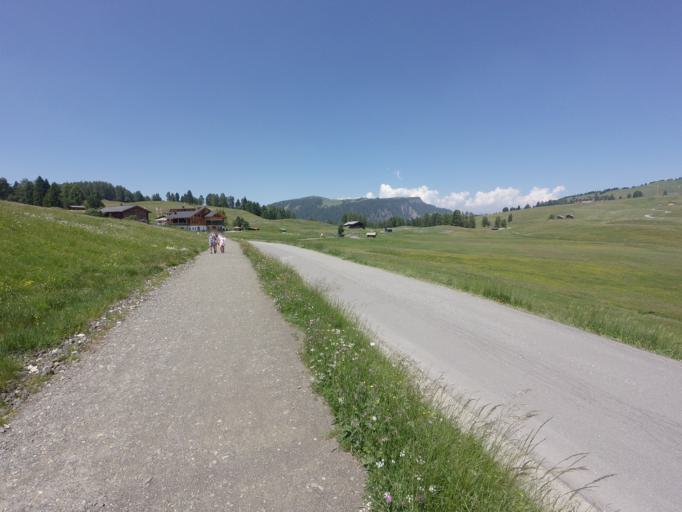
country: IT
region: Trentino-Alto Adige
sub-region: Bolzano
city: Ortisei
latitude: 46.5391
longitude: 11.6475
